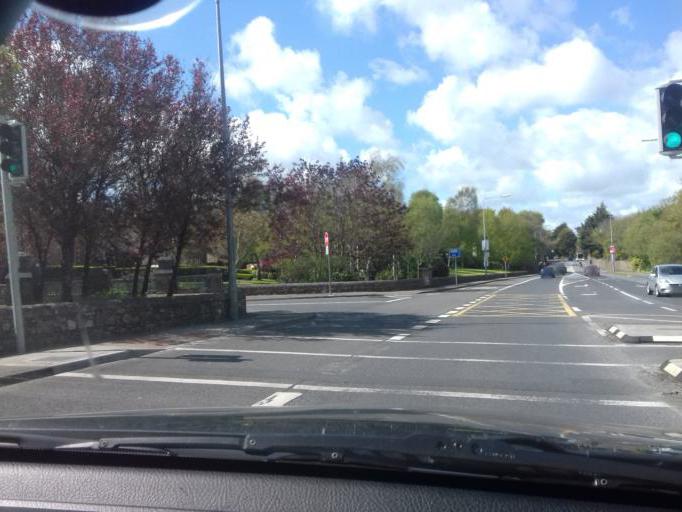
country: IE
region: Munster
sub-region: Waterford
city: Waterford
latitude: 52.2423
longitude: -7.0698
